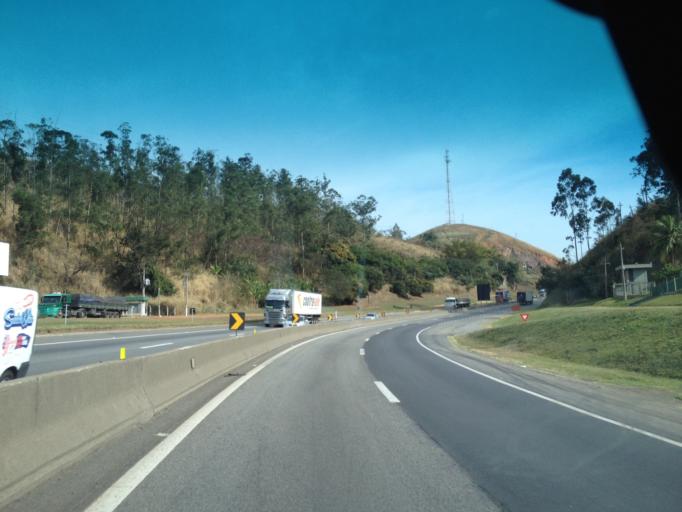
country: BR
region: Rio de Janeiro
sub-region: Barra Mansa
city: Barra Mansa
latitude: -22.5449
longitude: -44.1881
